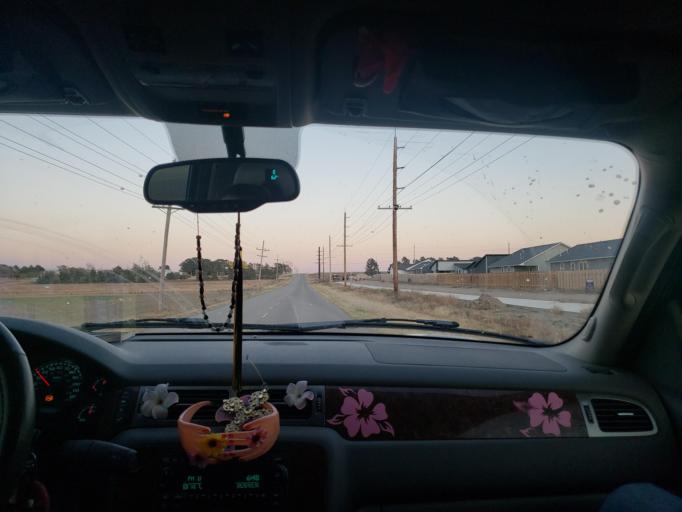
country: US
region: Kansas
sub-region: Finney County
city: Garden City
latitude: 37.9888
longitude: -100.8216
